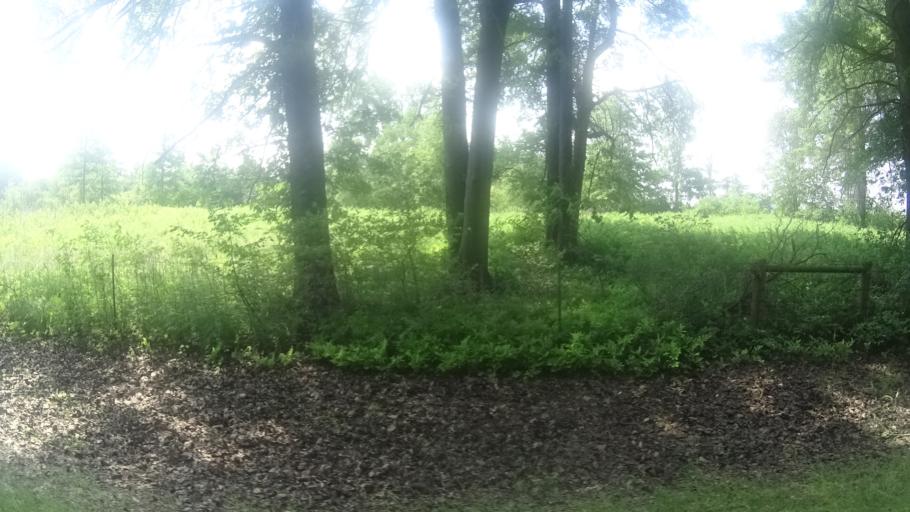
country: US
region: Ohio
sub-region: Erie County
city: Sandusky
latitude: 41.3597
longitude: -82.7112
